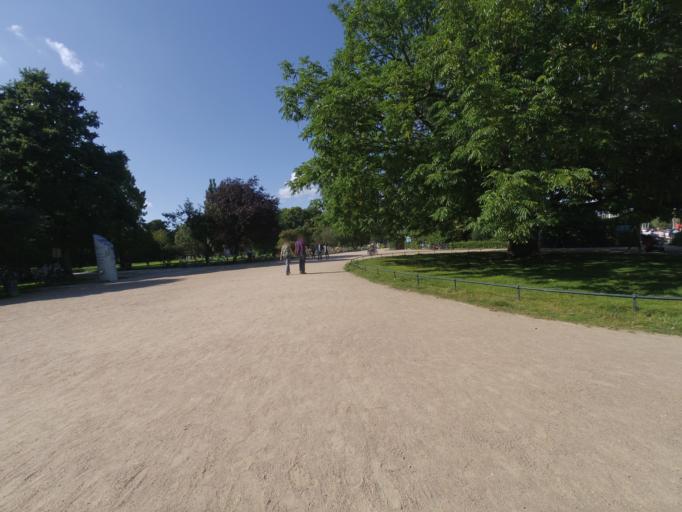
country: DE
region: Hamburg
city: Hamburg
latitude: 53.5734
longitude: 10.0024
